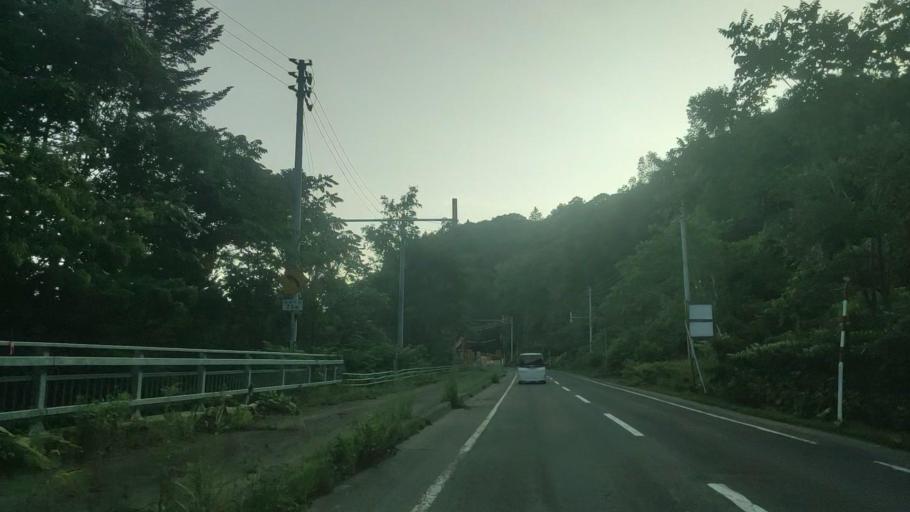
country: JP
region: Hokkaido
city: Bibai
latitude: 43.2379
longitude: 142.0350
